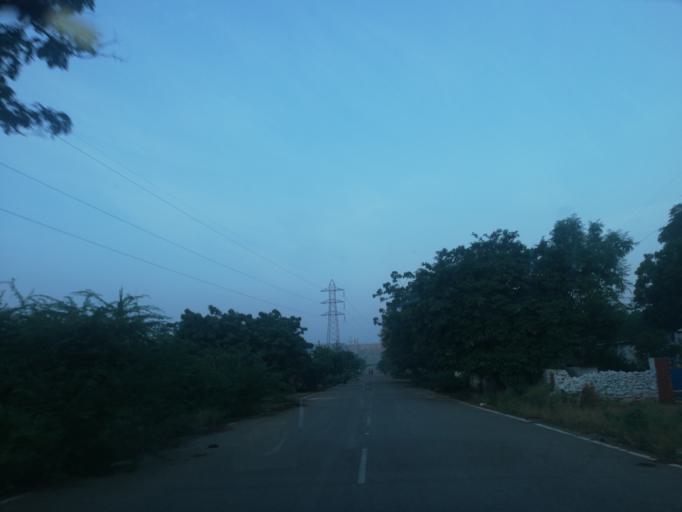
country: IN
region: Andhra Pradesh
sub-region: Guntur
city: Macherla
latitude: 16.5808
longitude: 79.3240
